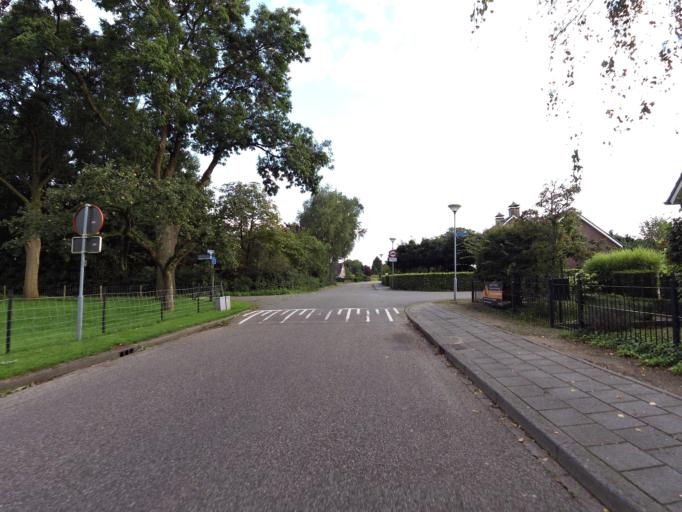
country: NL
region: Gelderland
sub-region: Gemeente Montferland
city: s-Heerenberg
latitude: 51.8842
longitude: 6.2666
